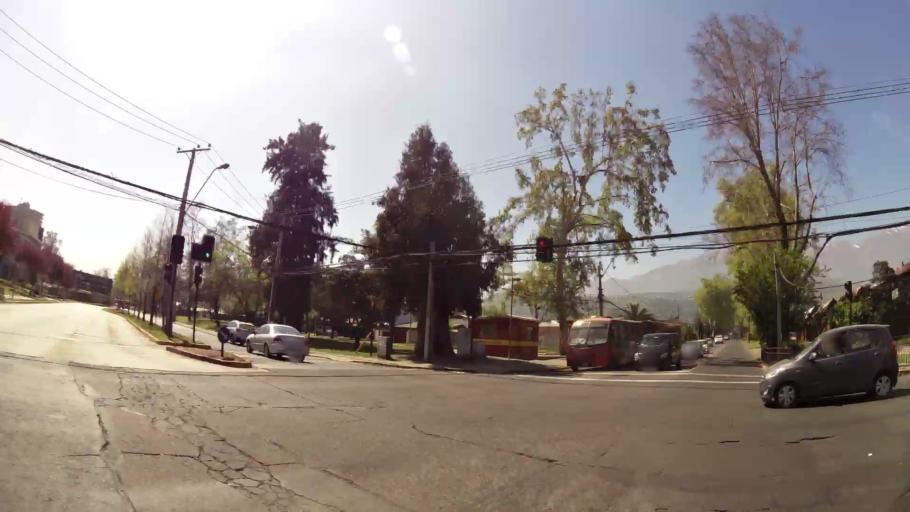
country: CL
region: Santiago Metropolitan
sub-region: Provincia de Santiago
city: Villa Presidente Frei, Nunoa, Santiago, Chile
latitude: -33.4236
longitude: -70.5382
